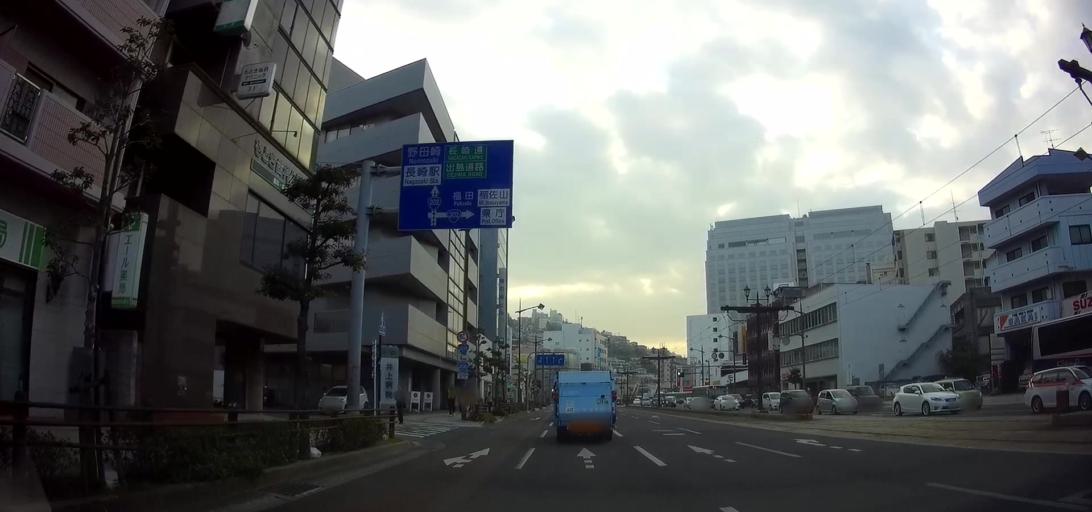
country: JP
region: Nagasaki
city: Nagasaki-shi
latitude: 32.7594
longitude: 129.8666
